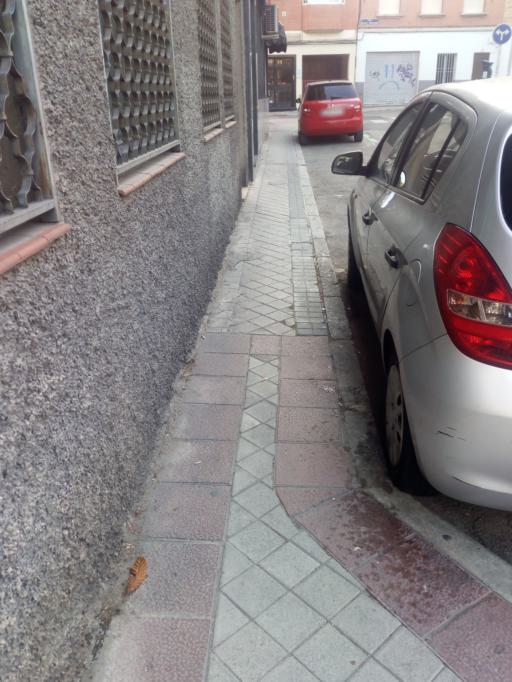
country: ES
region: Madrid
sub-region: Provincia de Madrid
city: Puente de Vallecas
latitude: 40.4027
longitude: -3.6686
